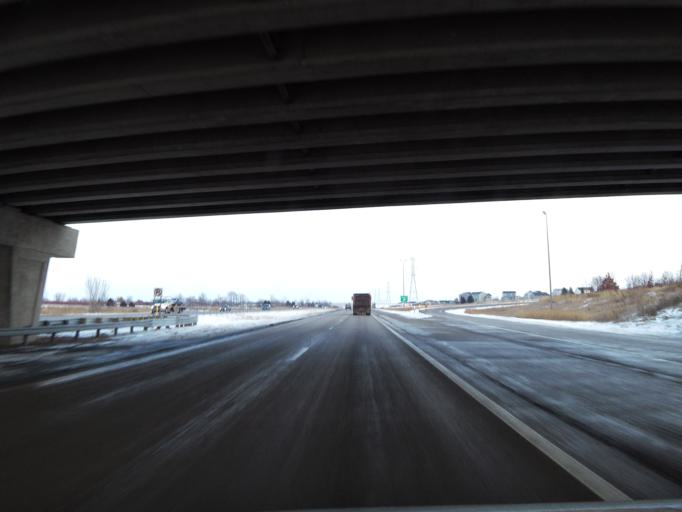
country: US
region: Minnesota
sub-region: Scott County
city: Shakopee
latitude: 44.7761
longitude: -93.5410
